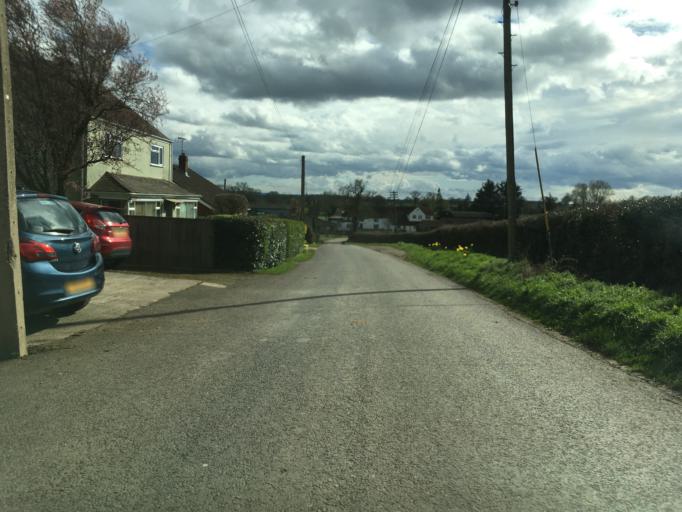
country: GB
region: England
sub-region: Gloucestershire
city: Newent
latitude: 51.8632
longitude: -2.3787
